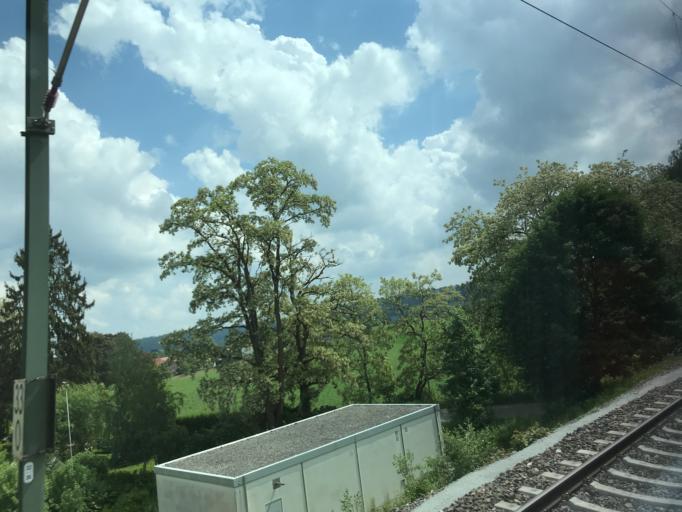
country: DE
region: Bavaria
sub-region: Swabia
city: Dinkelscherben
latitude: 48.3786
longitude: 10.5620
